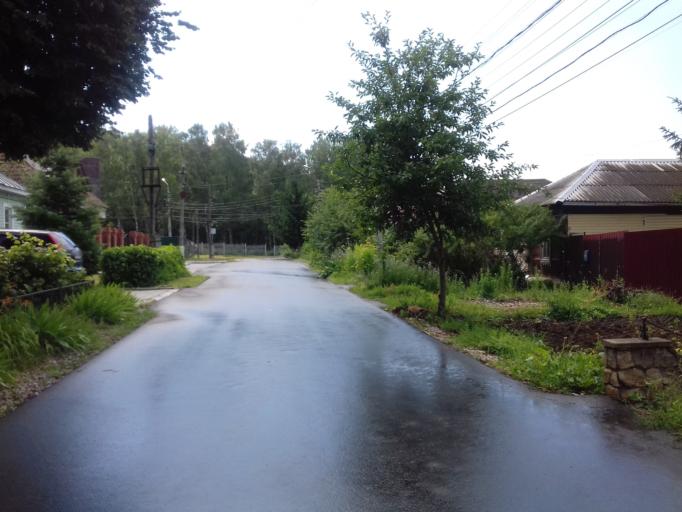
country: RU
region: Tula
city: Tula
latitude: 54.1867
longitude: 37.5814
